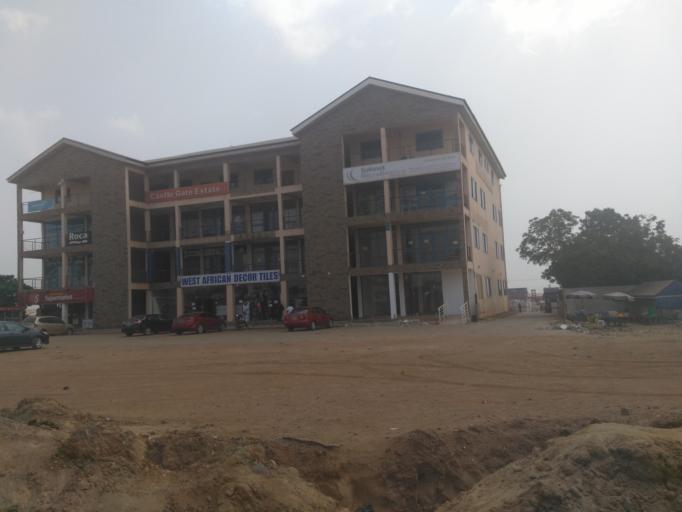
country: GH
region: Greater Accra
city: Tema
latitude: 5.6877
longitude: -0.0144
